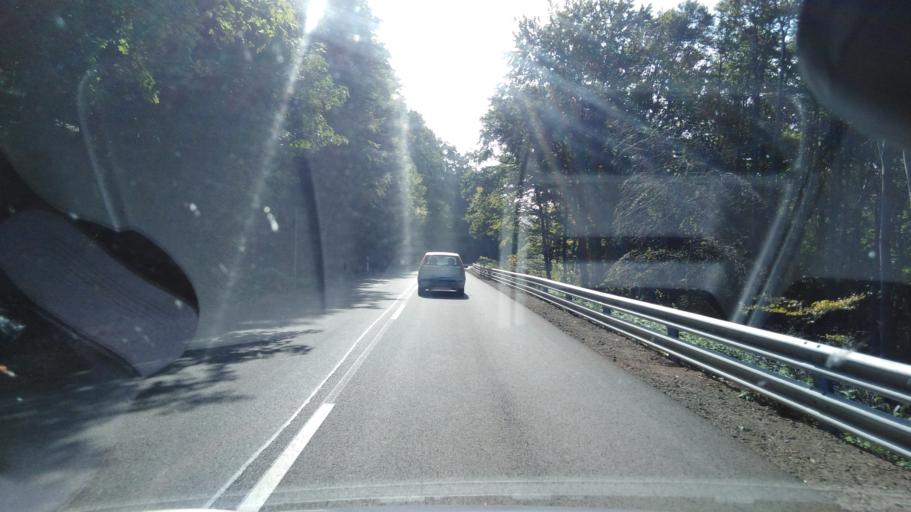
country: HU
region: Heves
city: Paradsasvar
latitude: 47.8729
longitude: 19.9804
